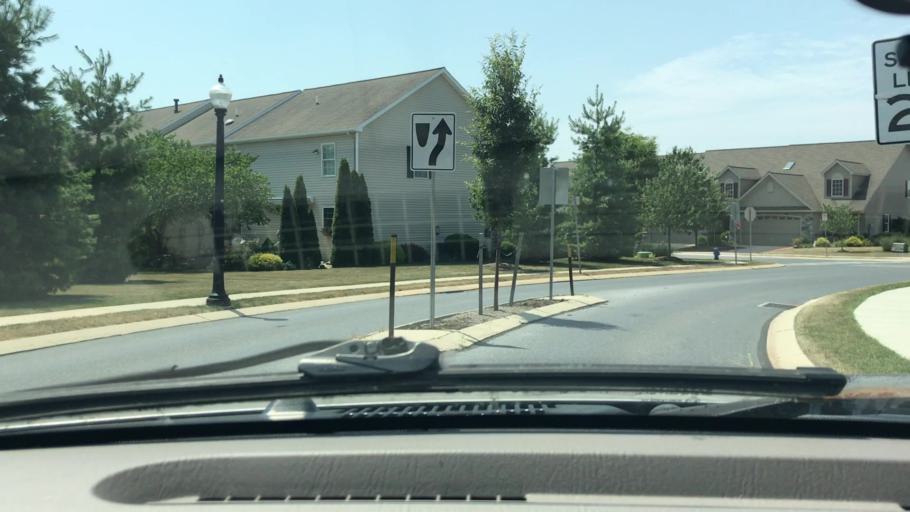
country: US
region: Pennsylvania
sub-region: Lancaster County
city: Mount Joy
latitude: 40.1141
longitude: -76.4808
